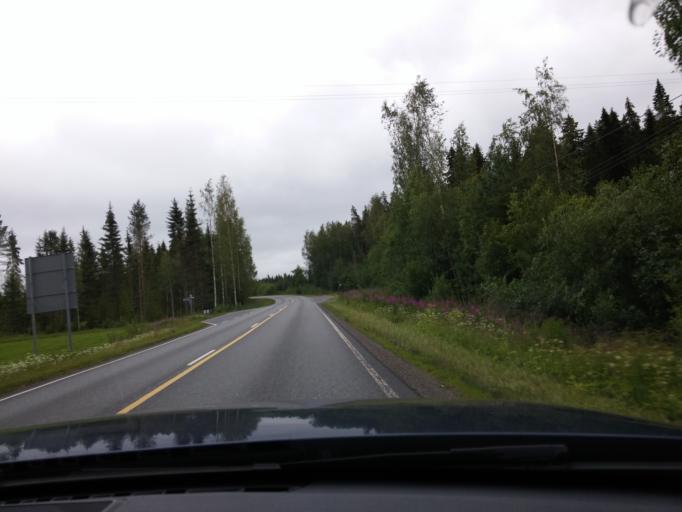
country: FI
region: Central Finland
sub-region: Joutsa
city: Luhanka
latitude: 61.8268
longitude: 25.9038
